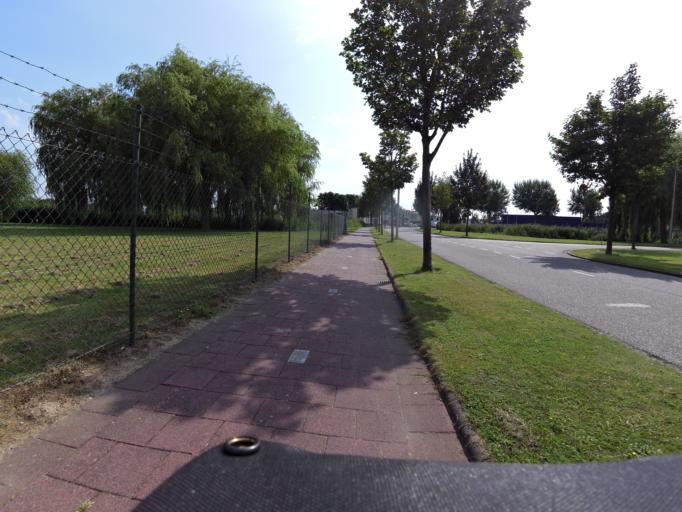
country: NL
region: South Holland
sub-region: Gemeente Oud-Beijerland
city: Oud-Beijerland
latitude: 51.8299
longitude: 4.4379
